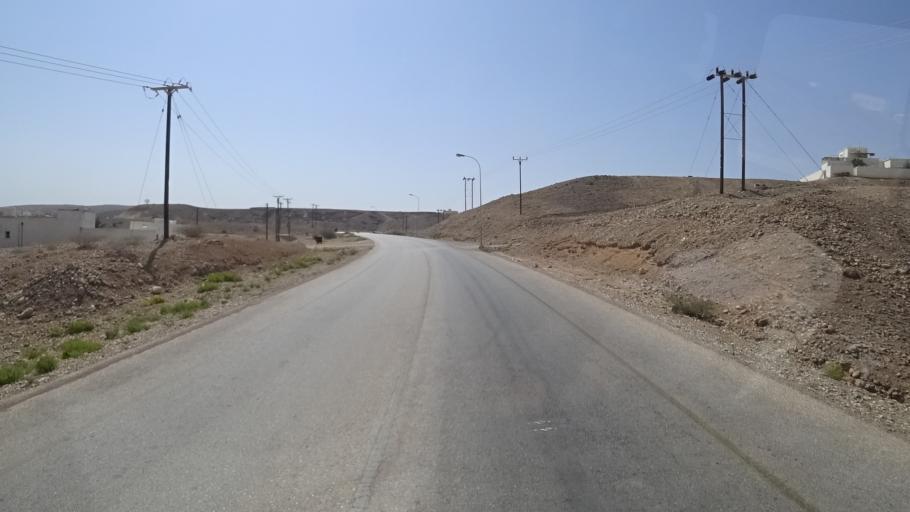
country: OM
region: Ash Sharqiyah
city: Sur
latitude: 22.5433
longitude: 59.5024
